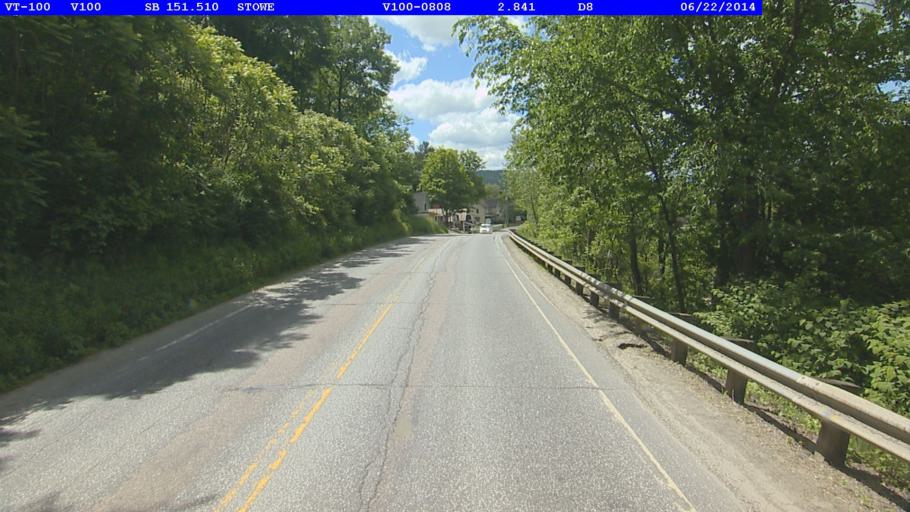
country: US
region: Vermont
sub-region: Lamoille County
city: Morristown
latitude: 44.4603
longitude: -72.6928
